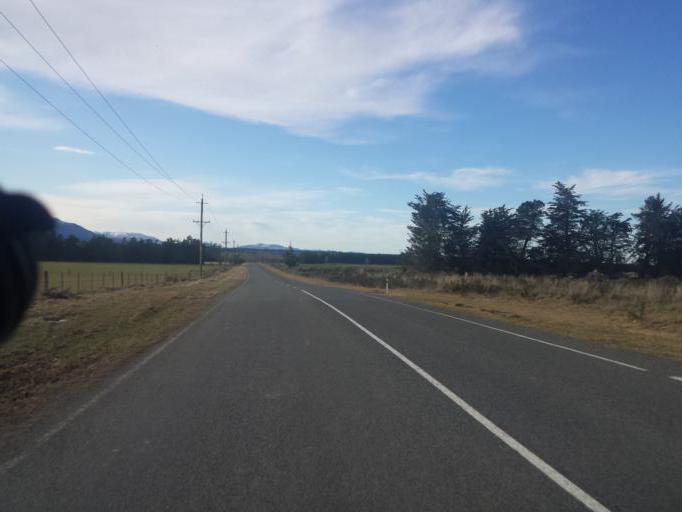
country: NZ
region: Canterbury
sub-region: Ashburton District
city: Methven
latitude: -43.6959
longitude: 171.4355
